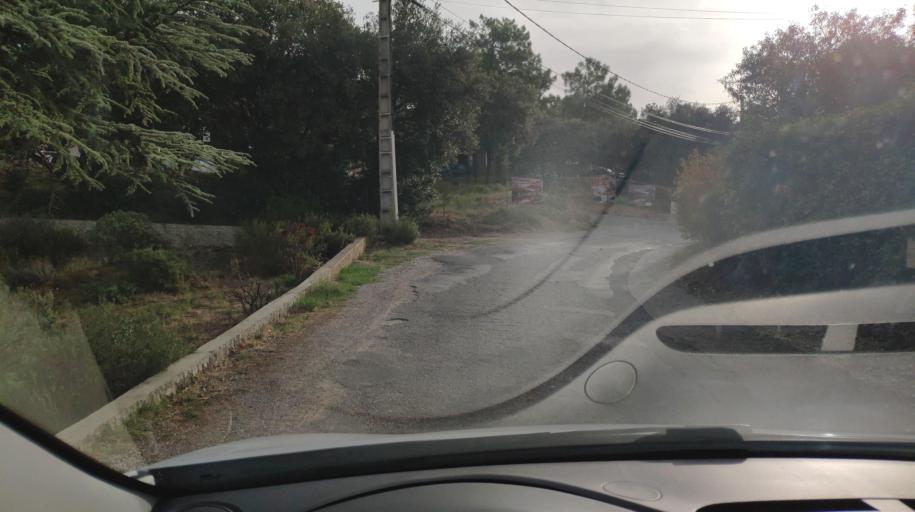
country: FR
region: Provence-Alpes-Cote d'Azur
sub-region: Departement du Vaucluse
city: Bedoin
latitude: 44.1189
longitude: 5.1816
